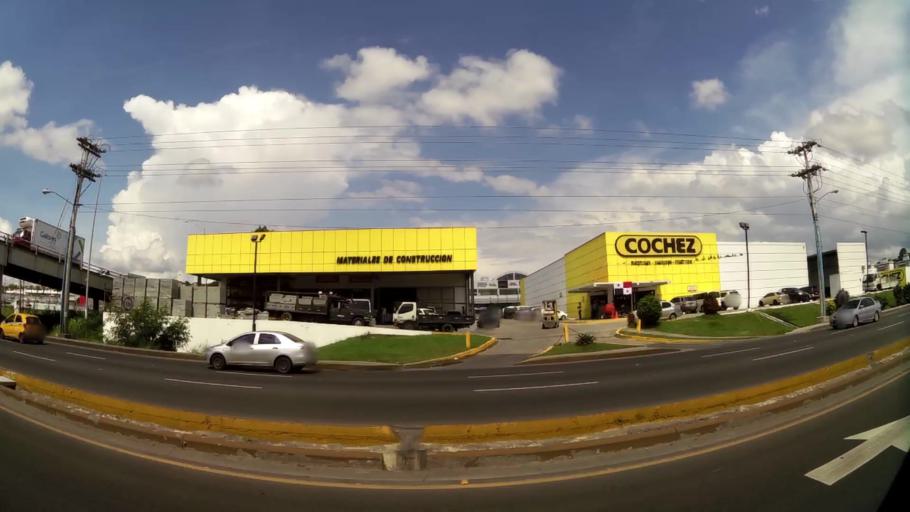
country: PA
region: Panama
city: San Miguelito
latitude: 9.0396
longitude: -79.4778
